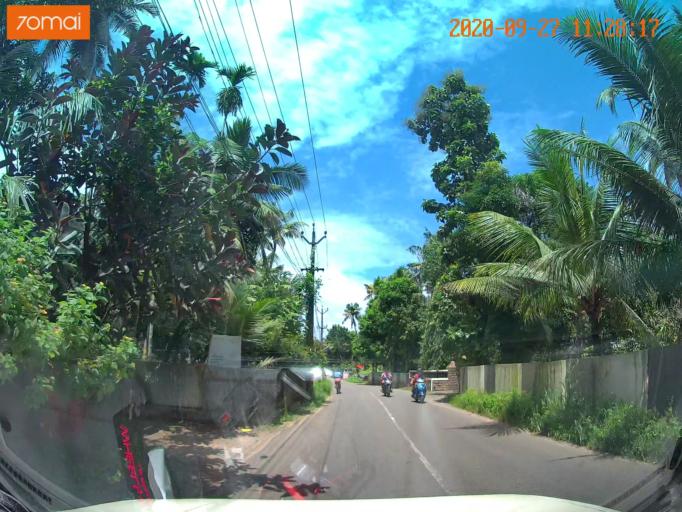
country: IN
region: Kerala
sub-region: Thrissur District
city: Thanniyam
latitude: 10.4155
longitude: 76.1402
